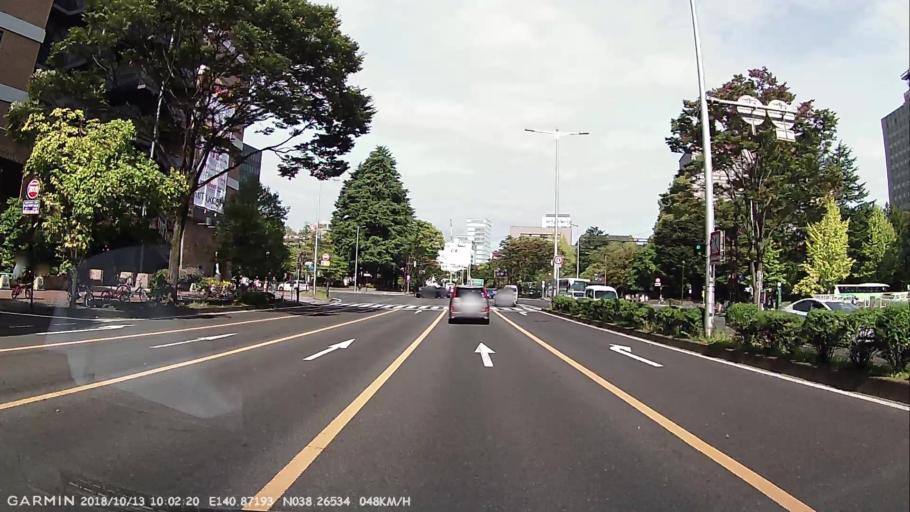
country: JP
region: Miyagi
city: Sendai-shi
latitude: 38.2654
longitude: 140.8719
